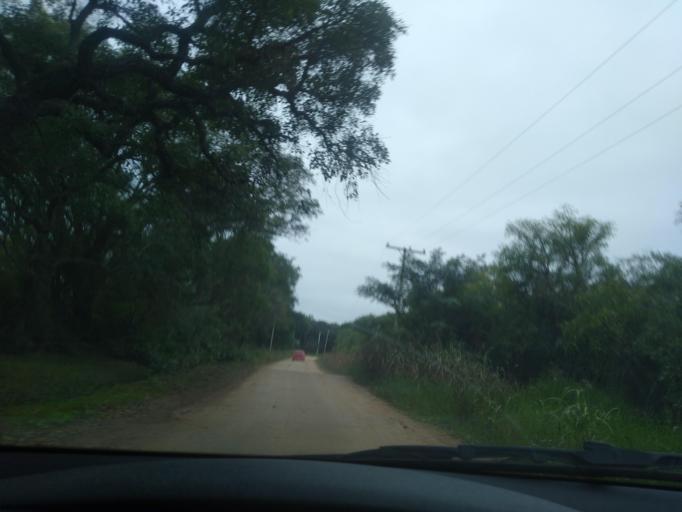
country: AR
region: Chaco
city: Colonia Benitez
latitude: -27.3354
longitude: -58.9601
